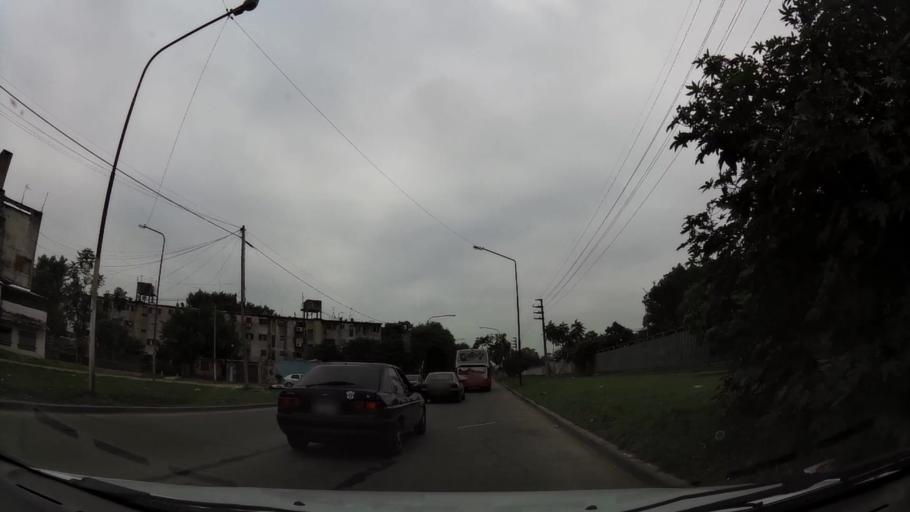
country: AR
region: Buenos Aires
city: San Justo
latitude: -34.7013
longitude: -58.5431
